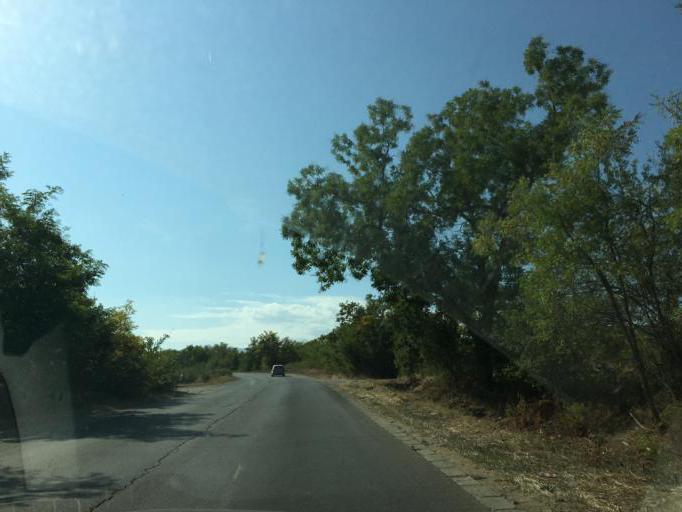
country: BG
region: Pazardzhik
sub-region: Obshtina Peshtera
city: Peshtera
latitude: 42.1091
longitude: 24.2970
